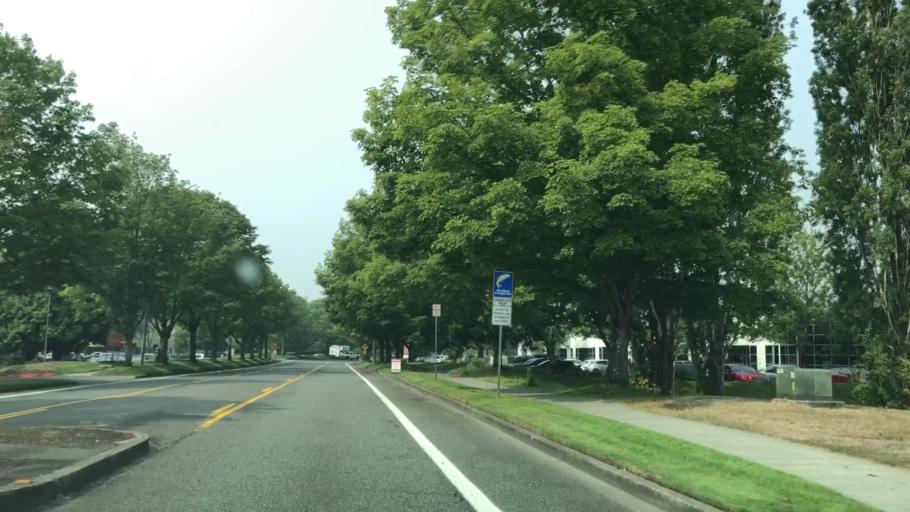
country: US
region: Washington
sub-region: King County
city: Woodinville
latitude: 47.7629
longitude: -122.1799
